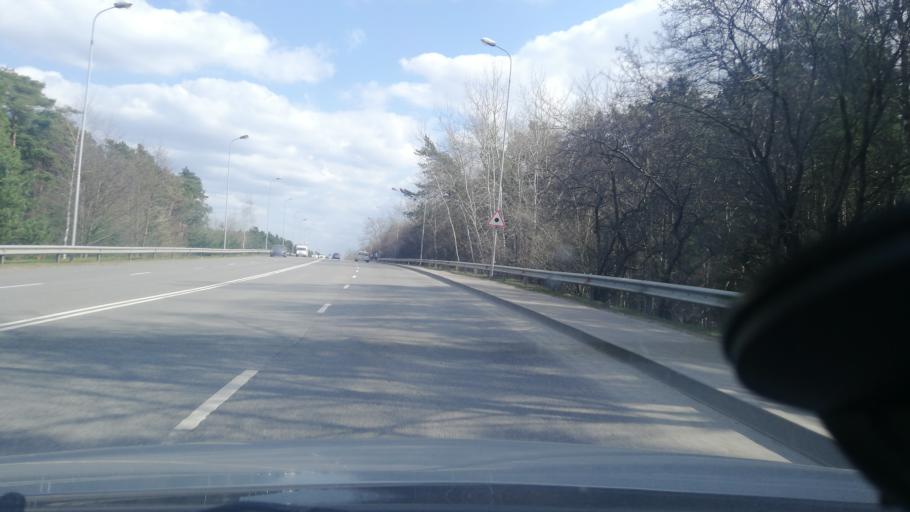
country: LT
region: Klaipedos apskritis
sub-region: Klaipeda
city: Klaipeda
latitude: 55.7343
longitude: 21.1037
